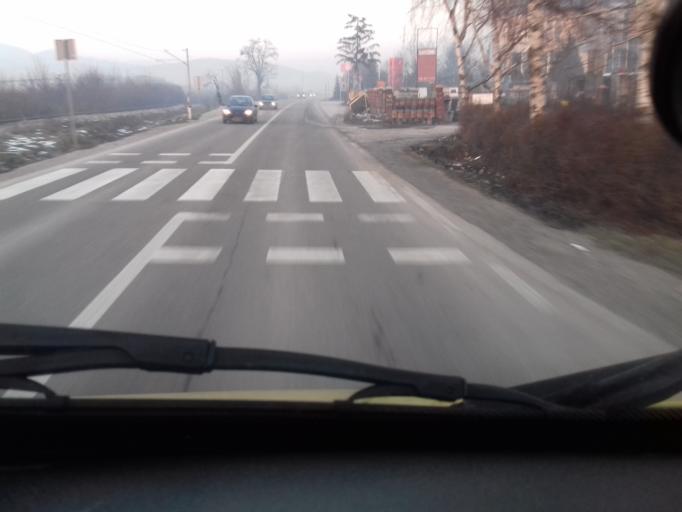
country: BA
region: Federation of Bosnia and Herzegovina
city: Vogosca
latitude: 43.8758
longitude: 18.3123
